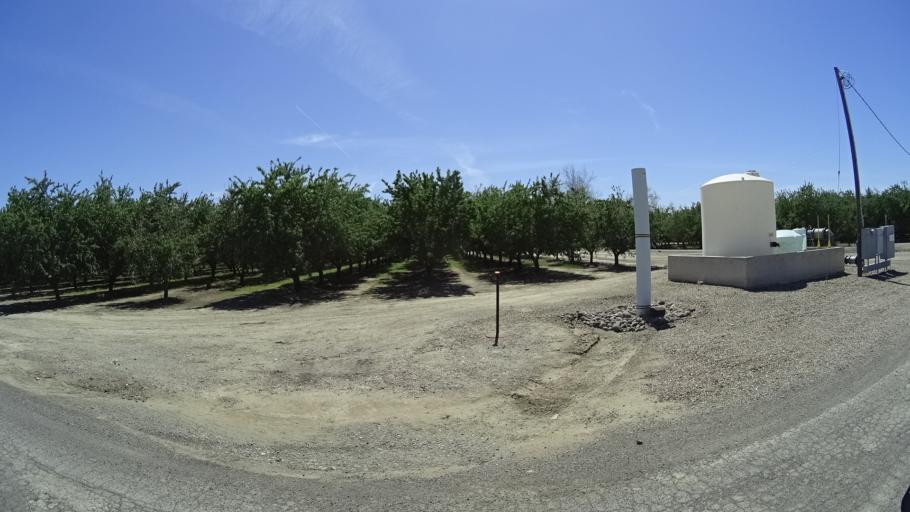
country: US
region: California
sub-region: Glenn County
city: Orland
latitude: 39.7323
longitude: -122.1320
